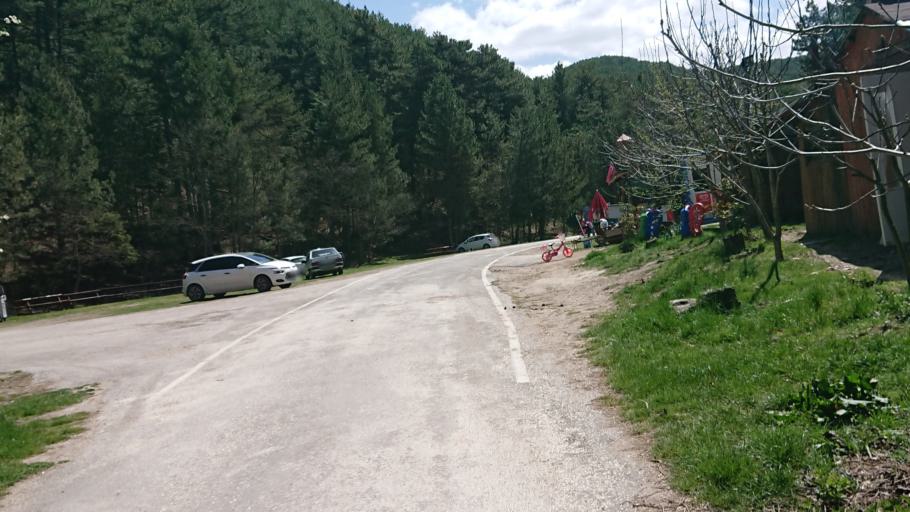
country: TR
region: Kuetahya
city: Sabuncu
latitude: 39.5141
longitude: 30.4242
